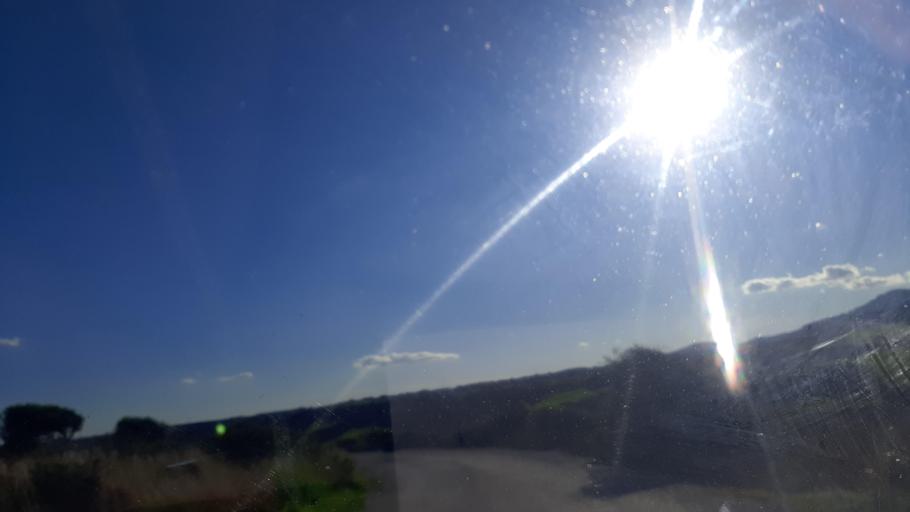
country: TN
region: Nabul
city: El Mida
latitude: 36.8355
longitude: 10.8346
